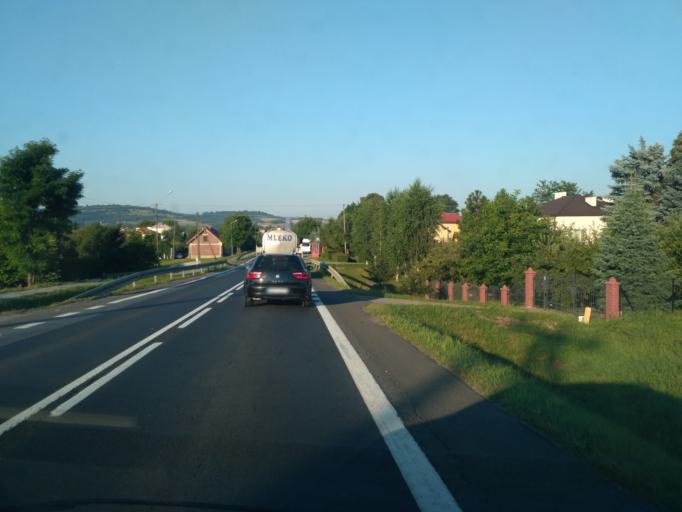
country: PL
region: Subcarpathian Voivodeship
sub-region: Powiat krosnienski
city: Miejsce Piastowe
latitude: 49.6249
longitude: 21.7693
